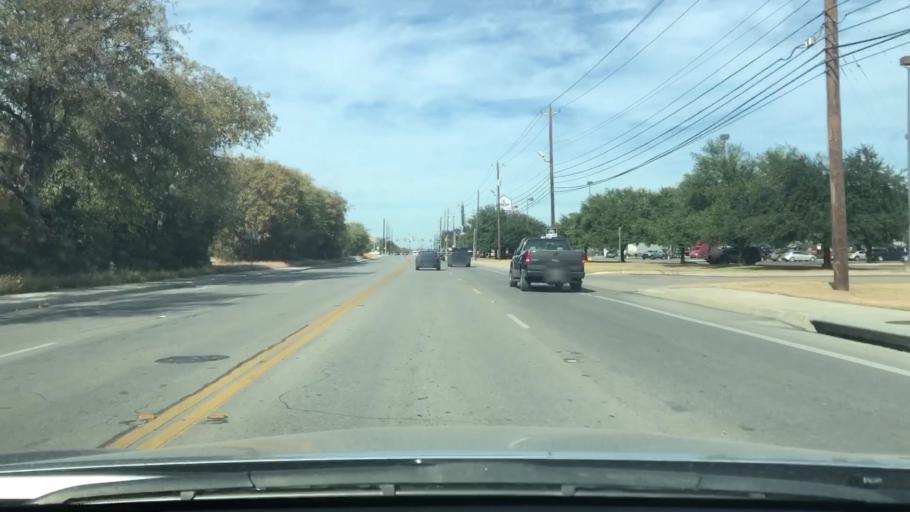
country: US
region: Texas
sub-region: Bexar County
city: Lackland Air Force Base
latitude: 29.4321
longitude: -98.5997
